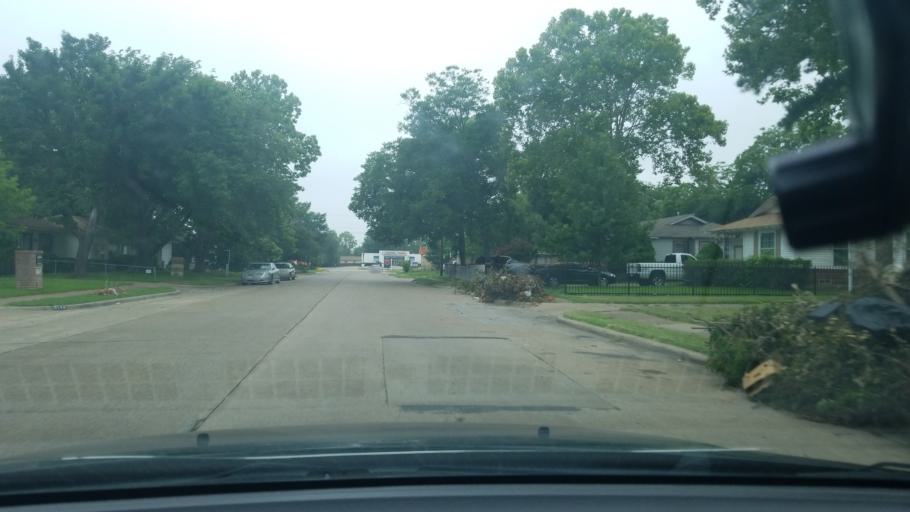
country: US
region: Texas
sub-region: Dallas County
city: Balch Springs
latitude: 32.7550
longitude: -96.6807
